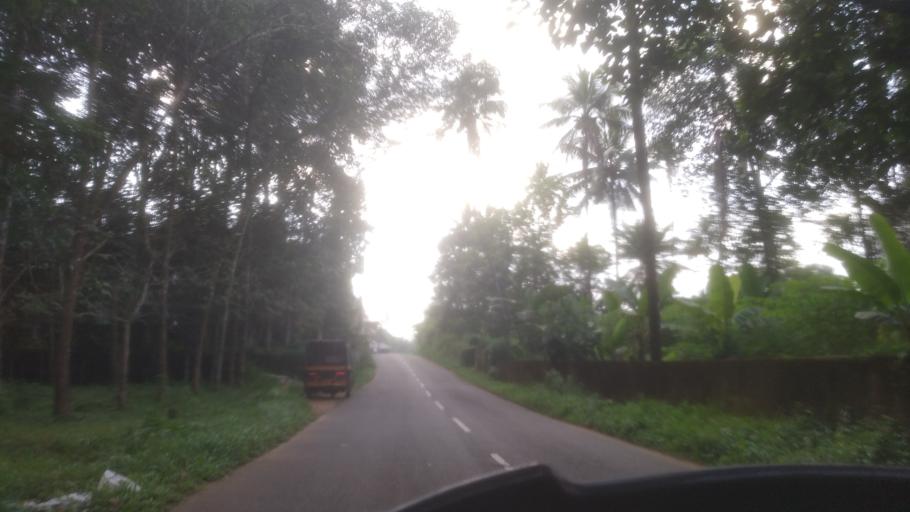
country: IN
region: Kerala
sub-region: Ernakulam
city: Kotamangalam
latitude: 10.0041
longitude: 76.6648
